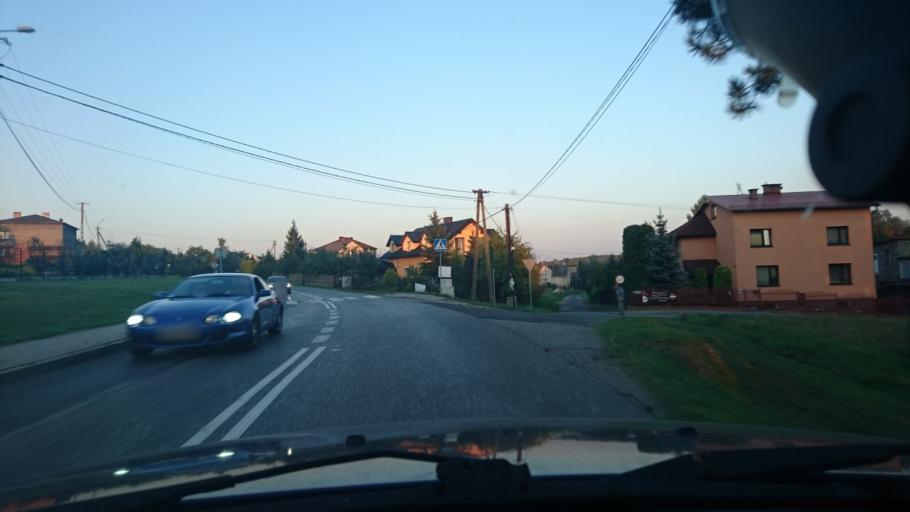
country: PL
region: Silesian Voivodeship
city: Janowice
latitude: 49.9012
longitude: 19.0794
